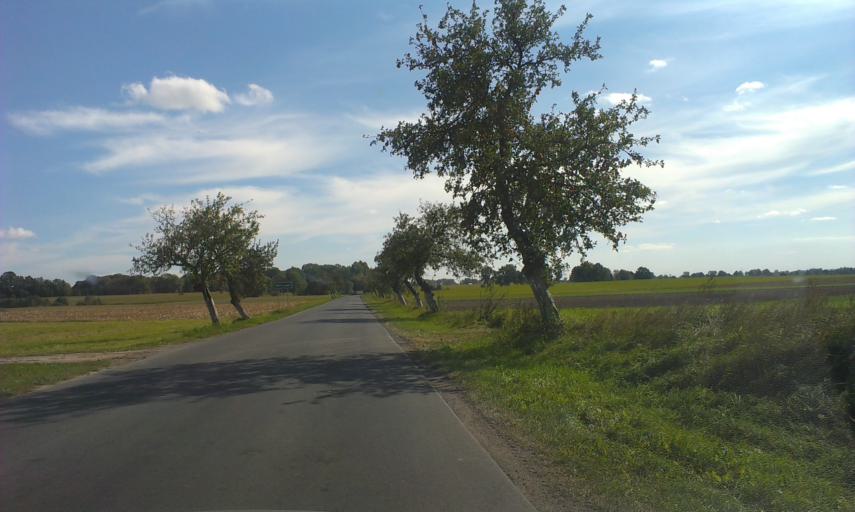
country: PL
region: Greater Poland Voivodeship
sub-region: Powiat pilski
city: Lobzenica
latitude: 53.2739
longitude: 17.2292
